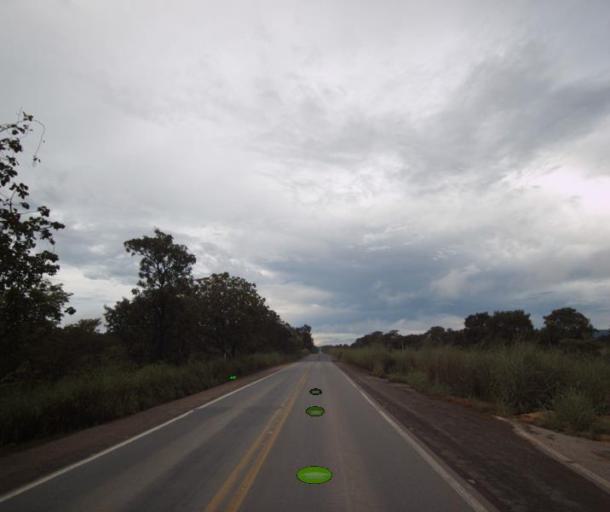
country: BR
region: Goias
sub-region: Porangatu
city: Porangatu
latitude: -13.5517
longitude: -49.0941
